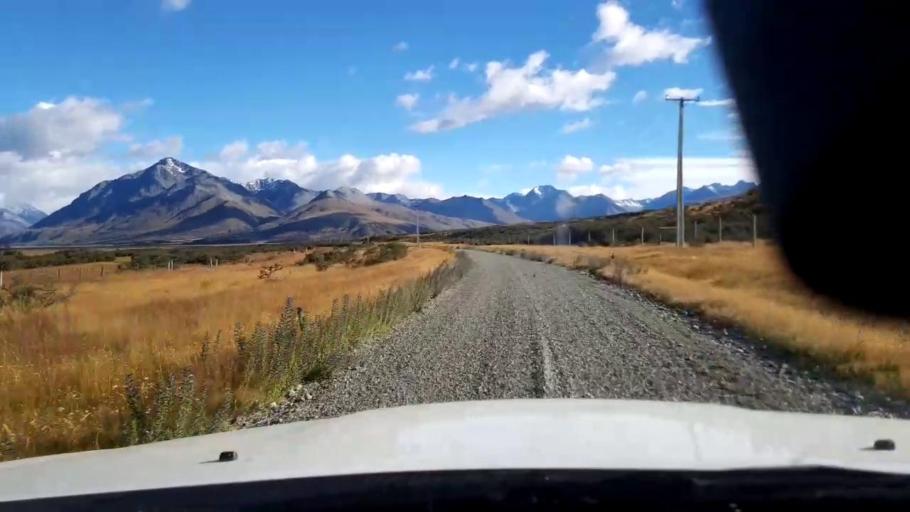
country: NZ
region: Canterbury
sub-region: Timaru District
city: Pleasant Point
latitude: -43.7665
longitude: 170.5695
